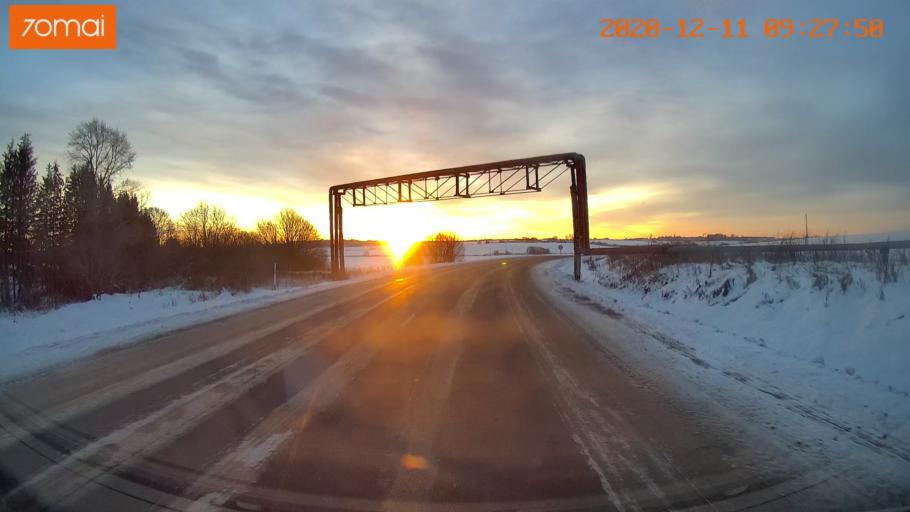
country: RU
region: Vologda
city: Vologda
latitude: 59.1595
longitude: 40.0098
